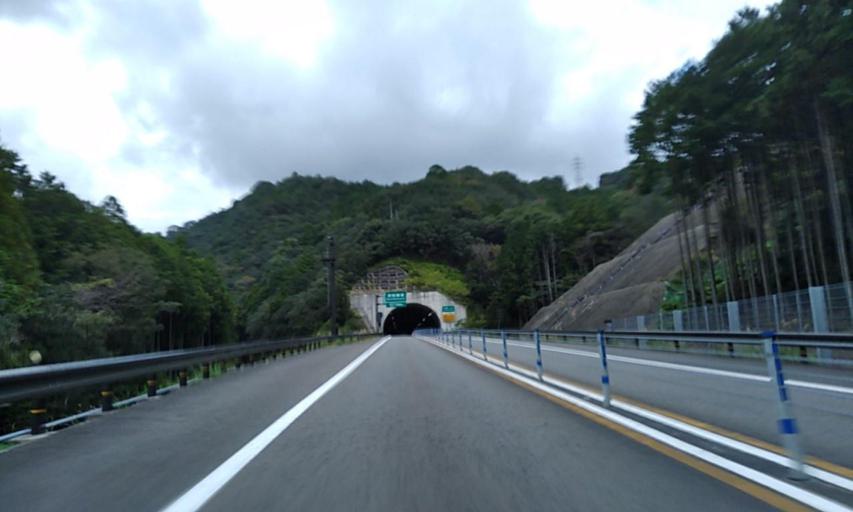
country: JP
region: Wakayama
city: Shingu
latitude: 33.6345
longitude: 135.9248
